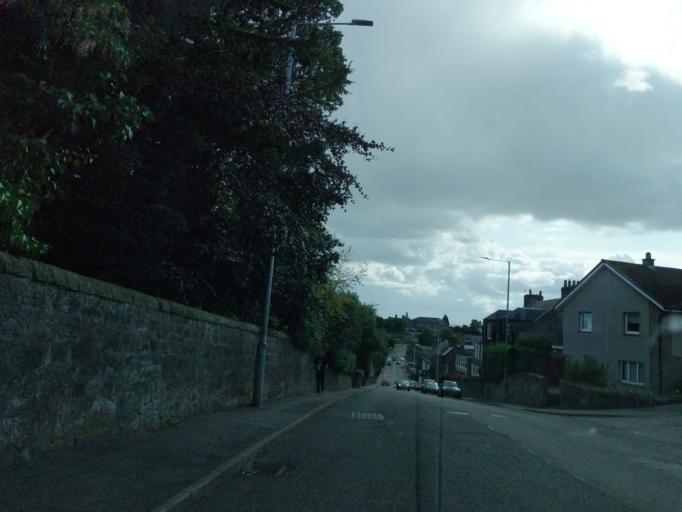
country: GB
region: Scotland
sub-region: Fife
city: Dunfermline
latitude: 56.0765
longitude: -3.4506
